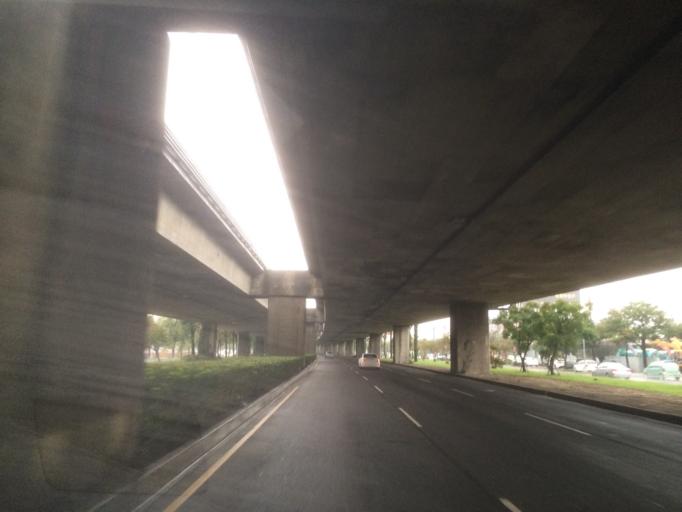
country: TW
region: Taiwan
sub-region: Taichung City
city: Taichung
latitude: 24.1583
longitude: 120.6263
